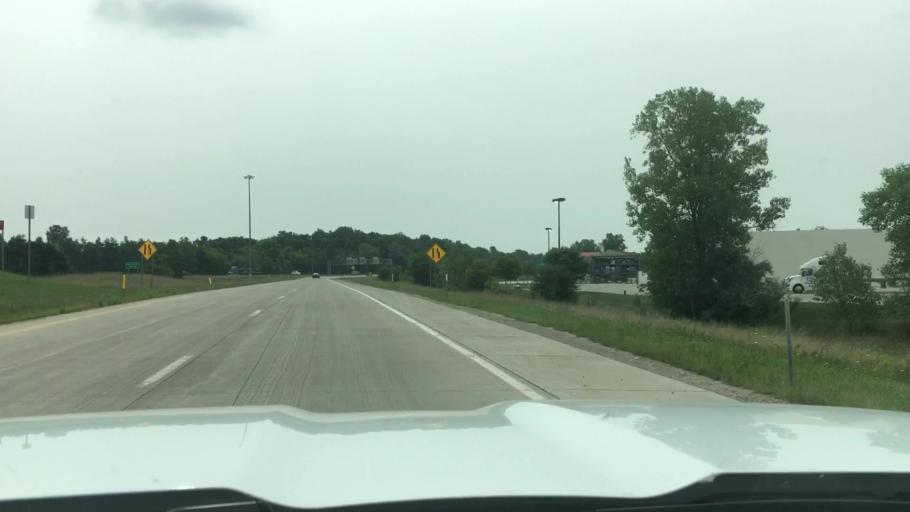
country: US
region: Michigan
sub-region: Eaton County
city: Waverly
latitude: 42.7407
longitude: -84.6698
